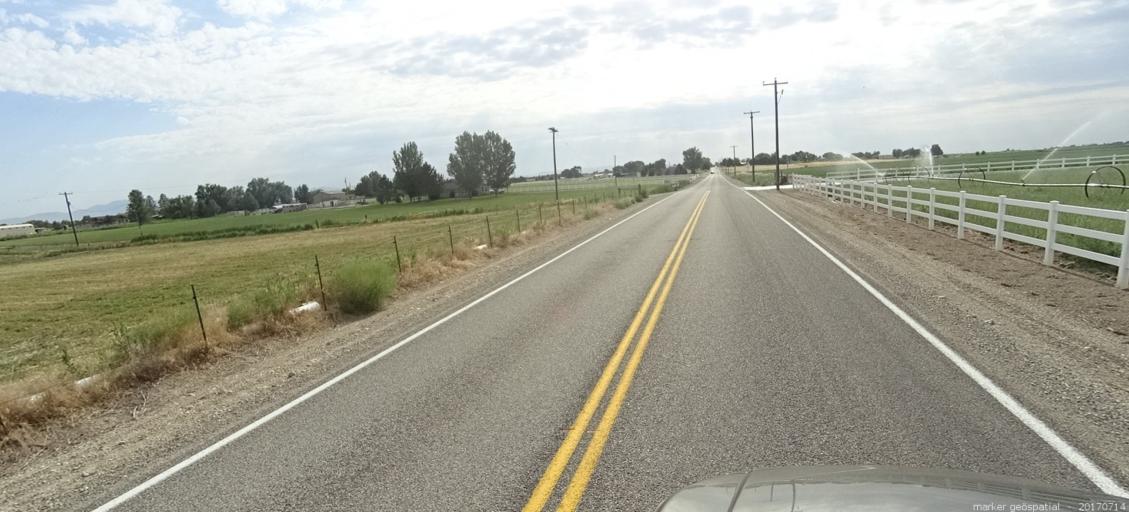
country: US
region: Idaho
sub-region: Ada County
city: Kuna
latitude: 43.4737
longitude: -116.3653
